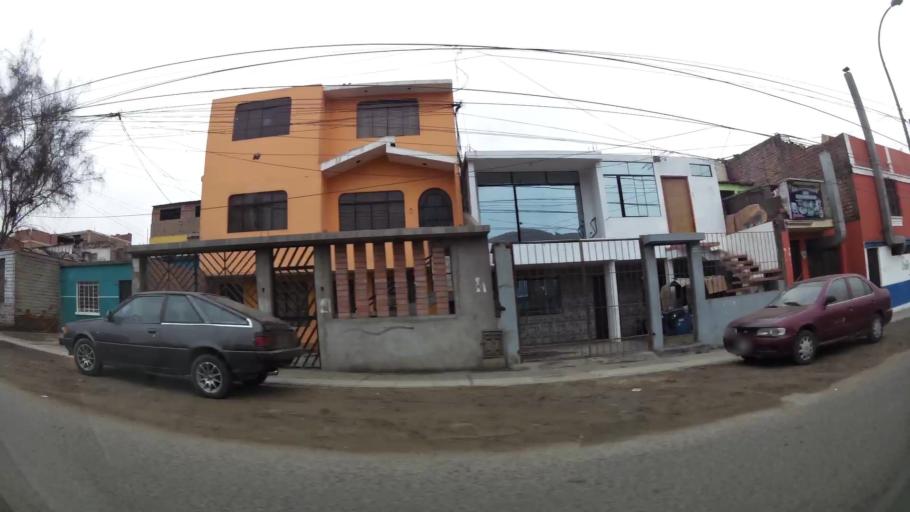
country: PE
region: Lima
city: Ventanilla
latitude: -11.8684
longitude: -77.1153
